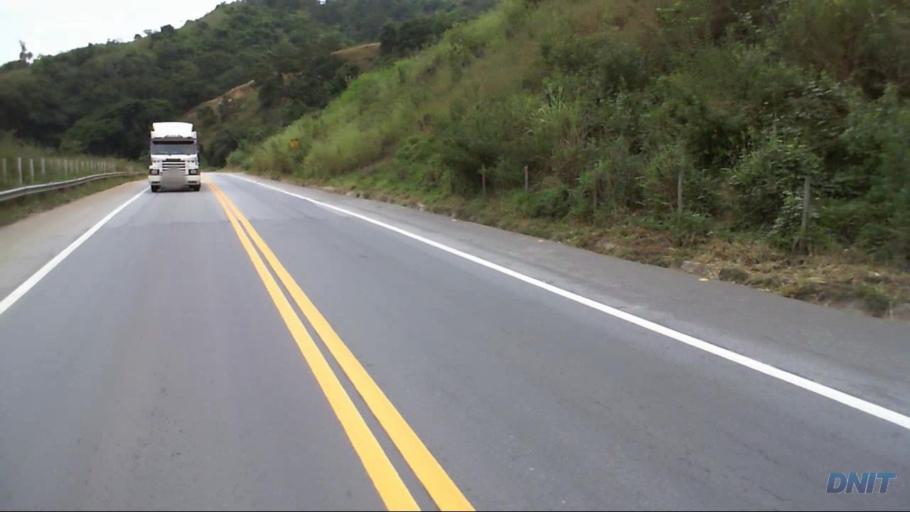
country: BR
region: Minas Gerais
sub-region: Timoteo
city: Timoteo
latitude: -19.6192
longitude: -42.7785
